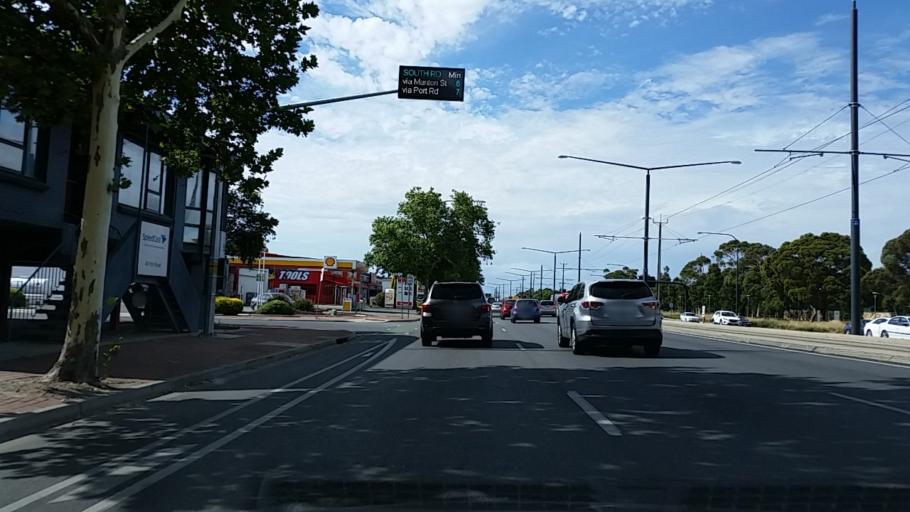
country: AU
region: South Australia
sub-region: City of West Torrens
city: Thebarton
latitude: -34.9157
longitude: 138.5781
